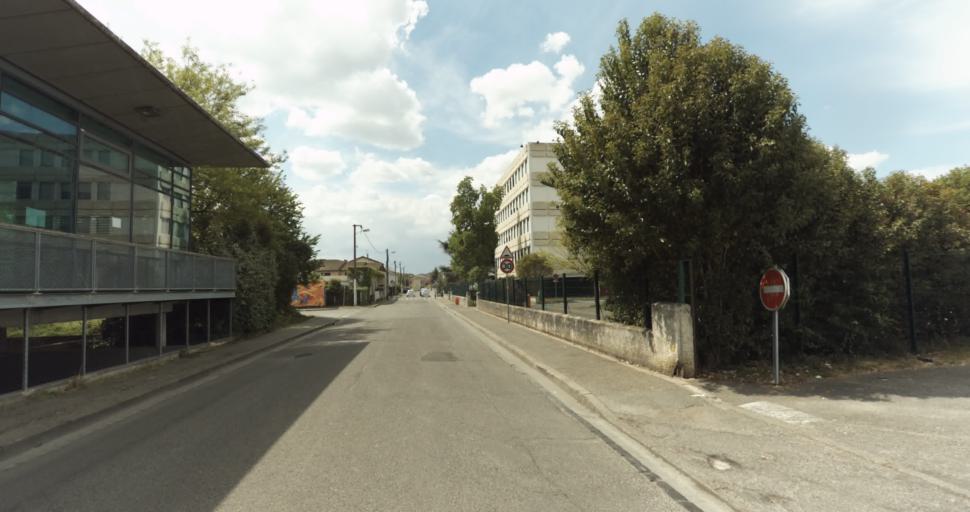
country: FR
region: Aquitaine
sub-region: Departement du Lot-et-Garonne
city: Agen
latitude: 44.1963
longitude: 0.6262
